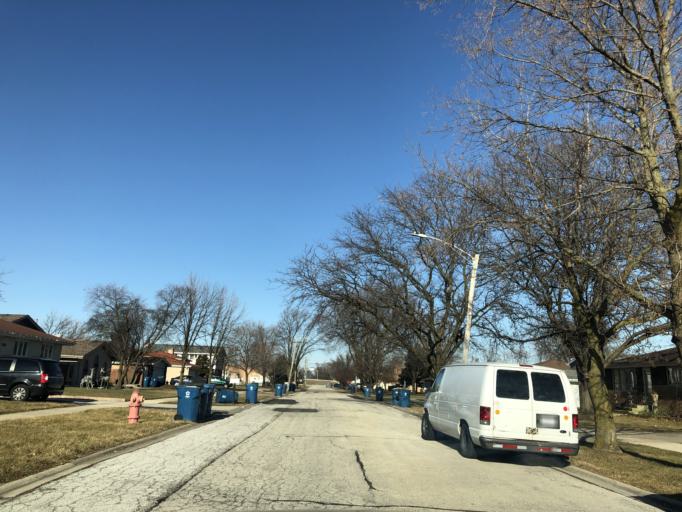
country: US
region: Illinois
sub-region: Cook County
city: Bridgeview
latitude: 41.7450
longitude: -87.8057
